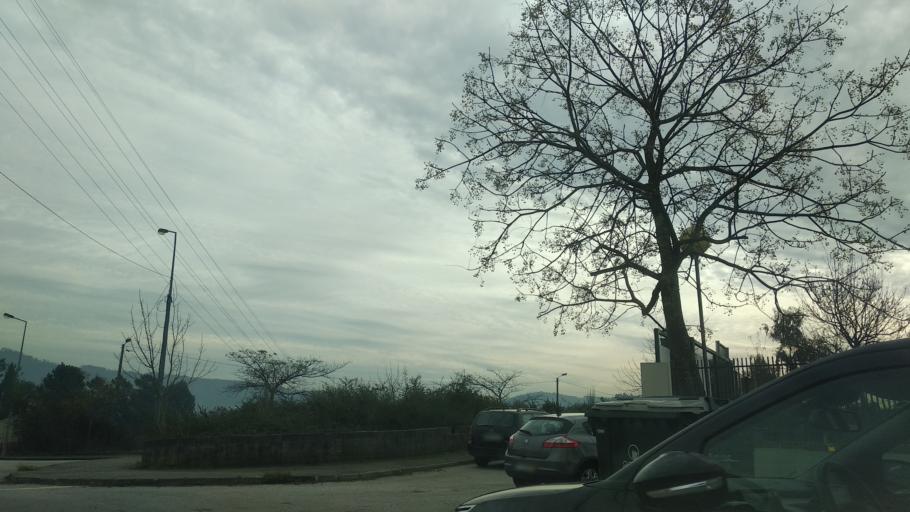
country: PT
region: Braga
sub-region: Braga
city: Braga
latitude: 41.5274
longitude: -8.4453
